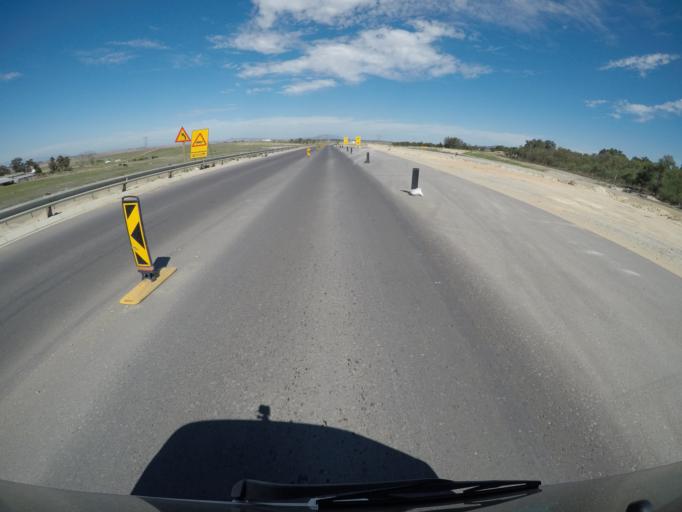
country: ZA
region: Western Cape
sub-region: West Coast District Municipality
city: Malmesbury
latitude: -33.5088
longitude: 18.6590
